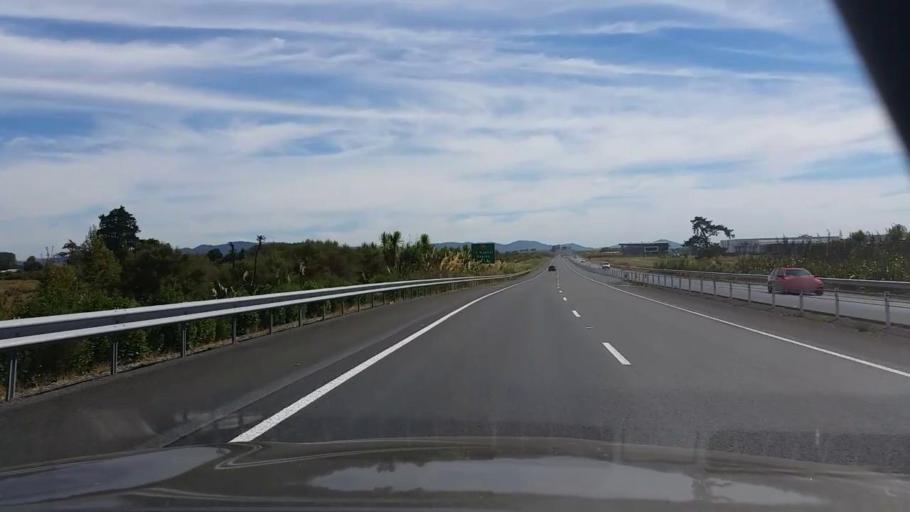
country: NZ
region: Waikato
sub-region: Hamilton City
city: Hamilton
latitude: -37.7468
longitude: 175.2153
